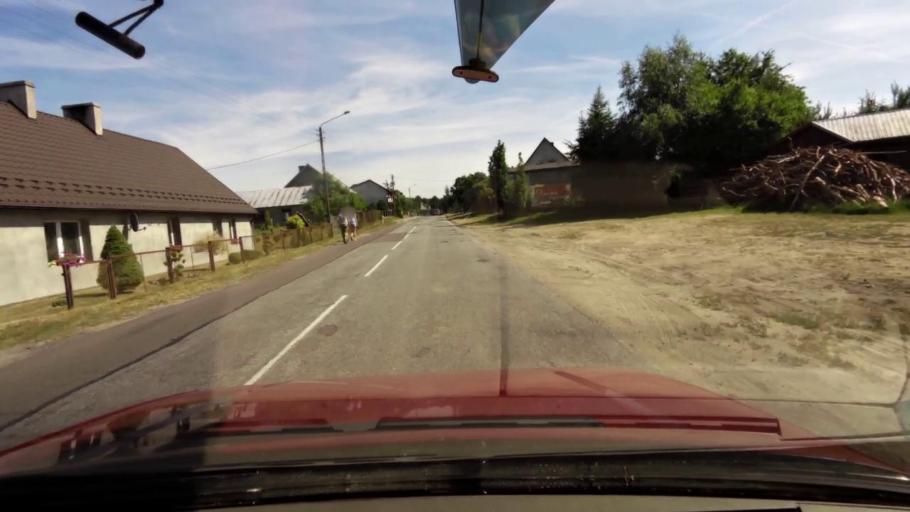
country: PL
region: Pomeranian Voivodeship
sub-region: Powiat slupski
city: Kepice
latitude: 54.2795
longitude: 16.9589
